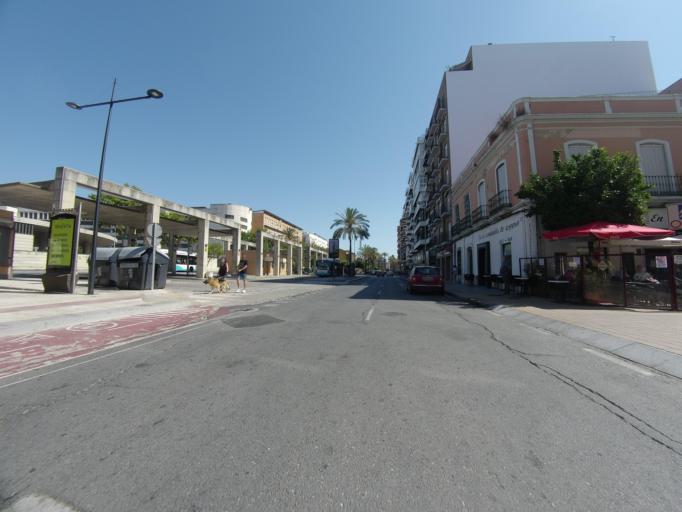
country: ES
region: Andalusia
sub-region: Provincia de Huelva
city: Huelva
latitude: 37.2572
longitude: -6.9566
